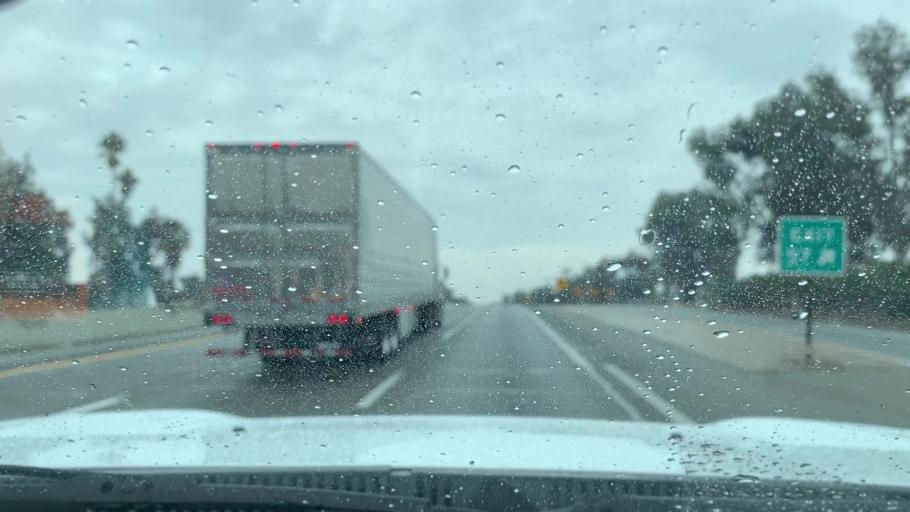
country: US
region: California
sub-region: Kern County
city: Delano
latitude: 35.7711
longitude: -119.2512
